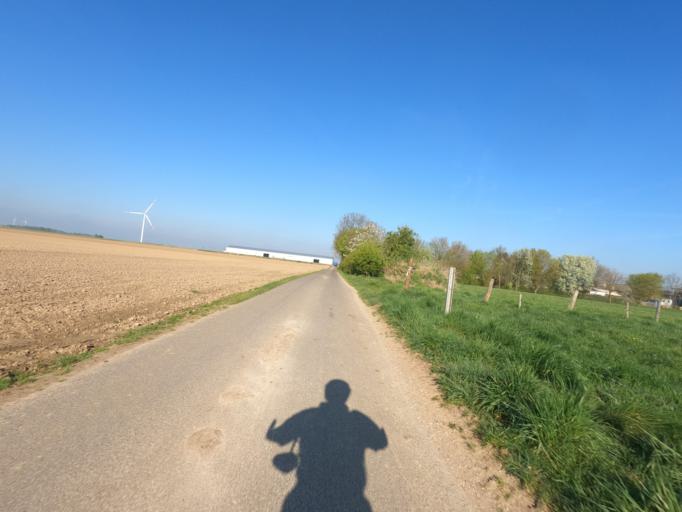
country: DE
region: North Rhine-Westphalia
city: Geilenkirchen
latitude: 51.0059
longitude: 6.0996
